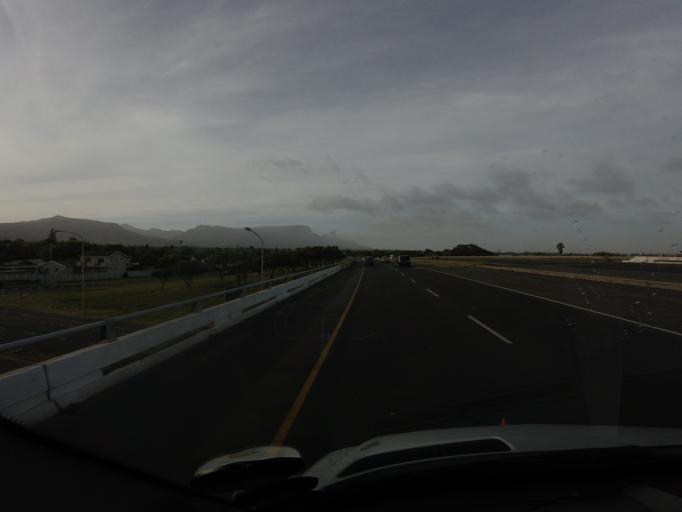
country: ZA
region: Western Cape
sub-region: City of Cape Town
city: Bergvliet
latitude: -34.0648
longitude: 18.4487
